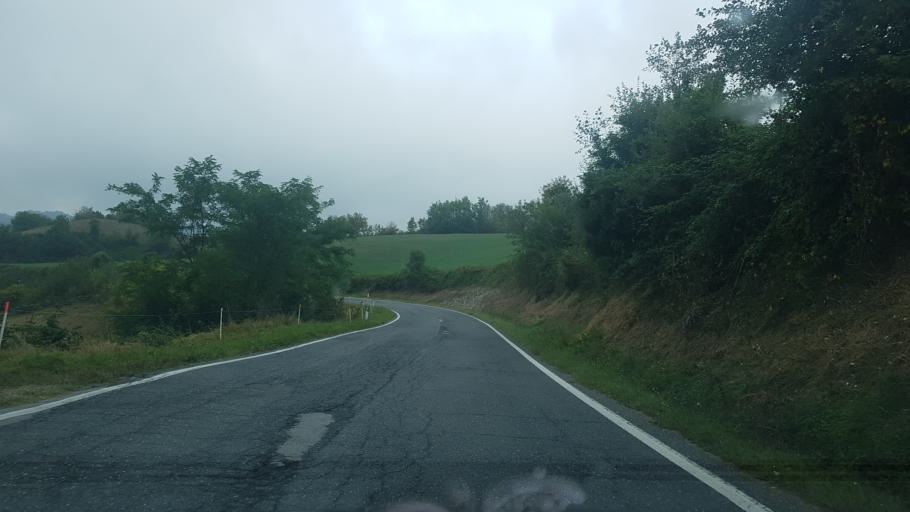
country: IT
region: Piedmont
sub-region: Provincia di Cuneo
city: Paroldo
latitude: 44.4311
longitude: 8.0851
